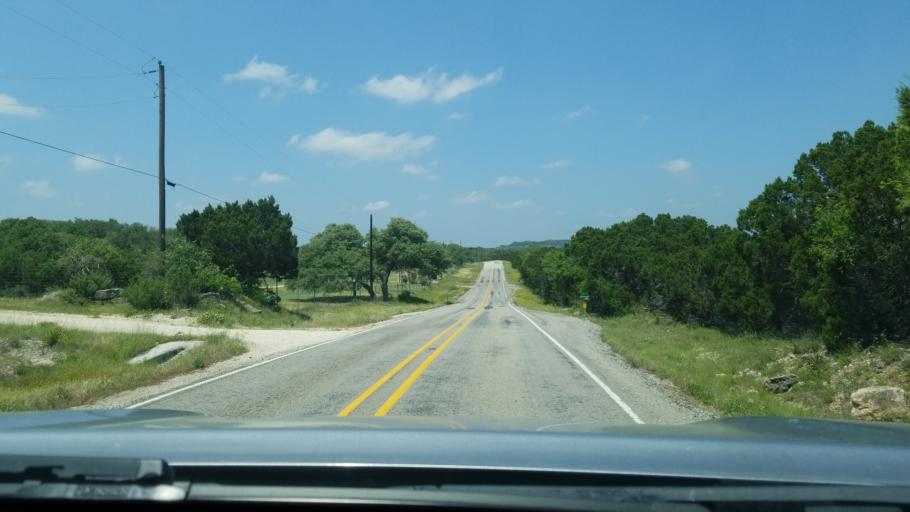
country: US
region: Texas
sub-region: Hays County
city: Woodcreek
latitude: 30.0871
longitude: -98.2283
